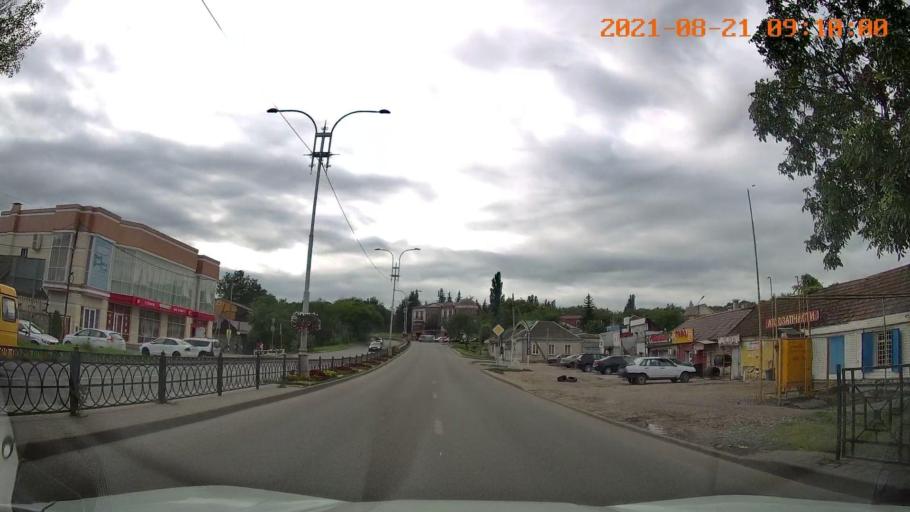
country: RU
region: Stavropol'skiy
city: Goryachevodskiy
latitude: 44.0268
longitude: 43.0737
